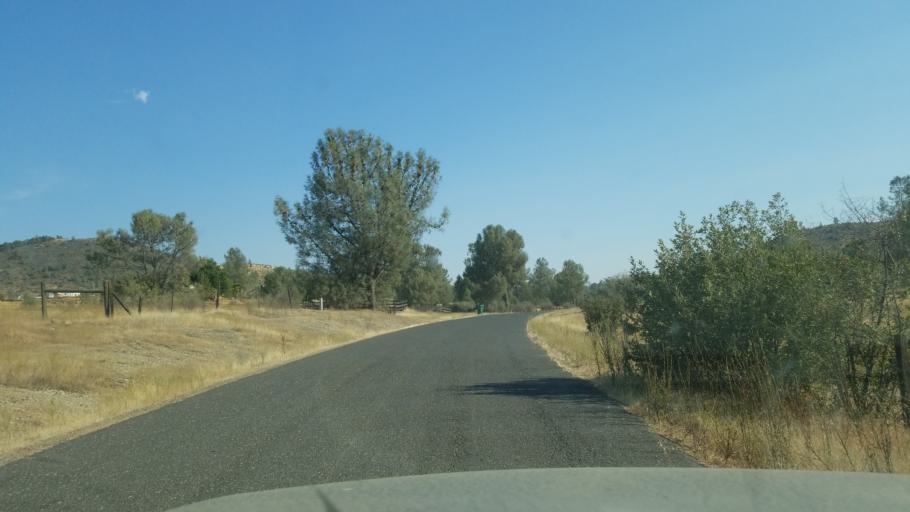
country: US
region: California
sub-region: Tuolumne County
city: Jamestown
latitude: 37.8660
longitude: -120.4538
